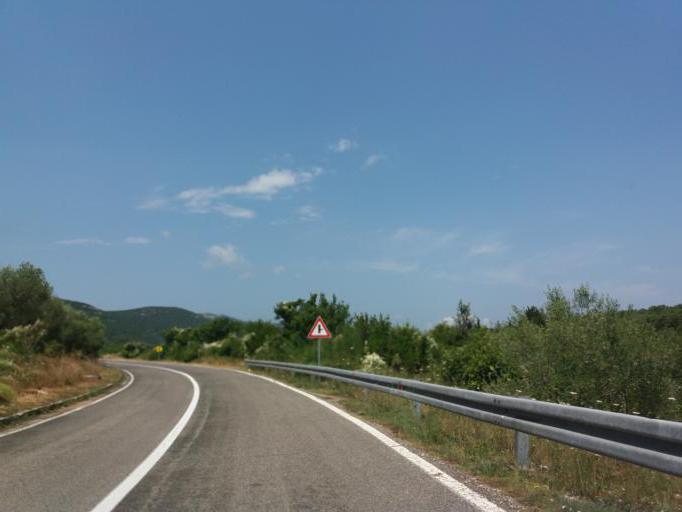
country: HR
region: Zadarska
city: Sali
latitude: 43.9755
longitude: 15.1074
